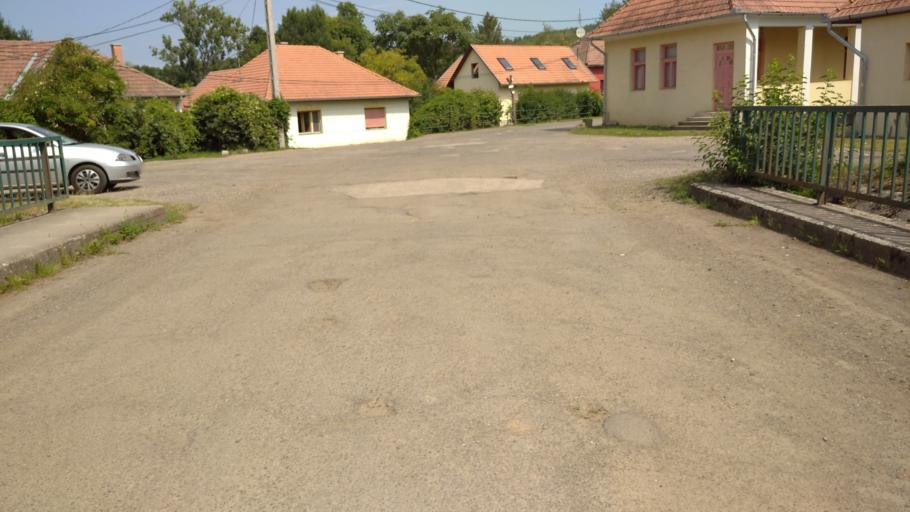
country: SK
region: Nitriansky
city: Sahy
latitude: 47.9941
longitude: 18.8628
